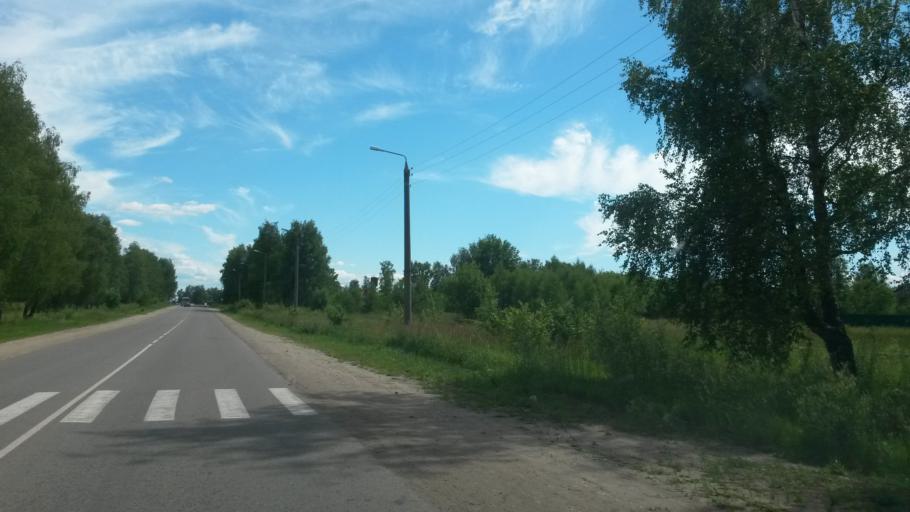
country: RU
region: Ivanovo
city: Zavolzhsk
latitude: 57.4702
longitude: 42.1595
